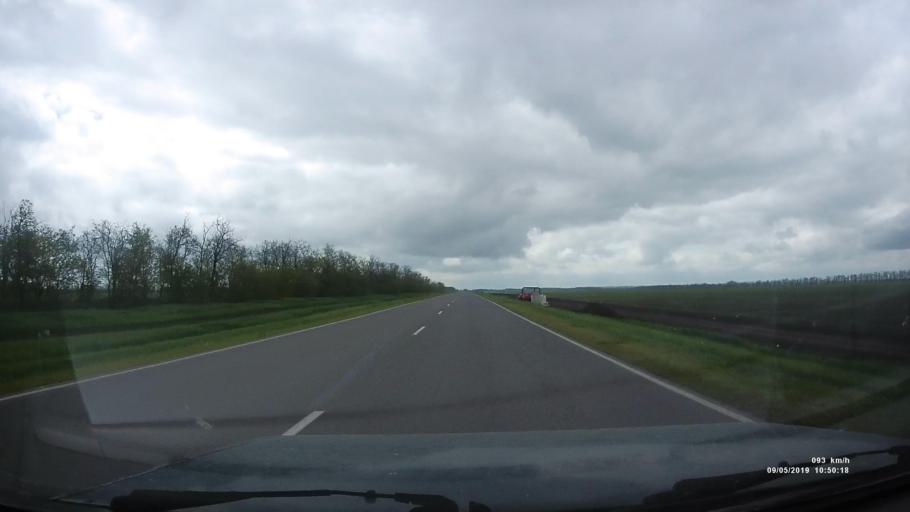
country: RU
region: Rostov
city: Peshkovo
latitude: 46.9305
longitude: 39.3554
